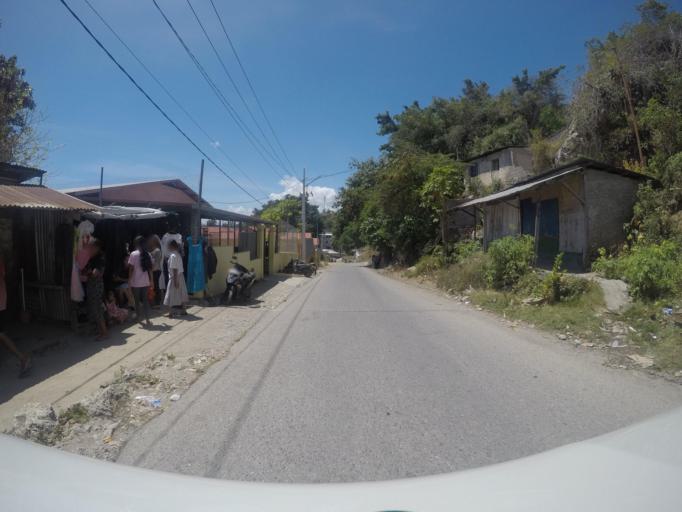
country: TL
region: Baucau
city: Baucau
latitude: -8.4627
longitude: 126.4502
